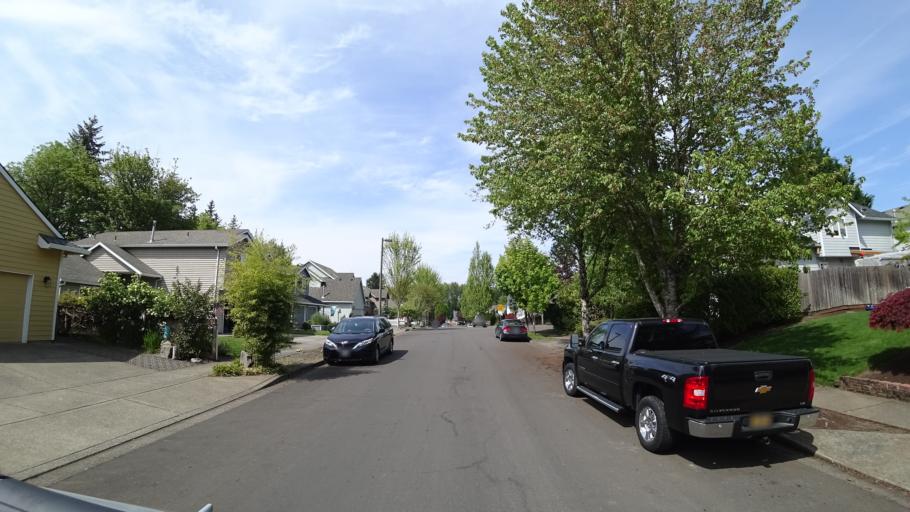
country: US
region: Oregon
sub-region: Washington County
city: Hillsboro
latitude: 45.5211
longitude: -122.9326
